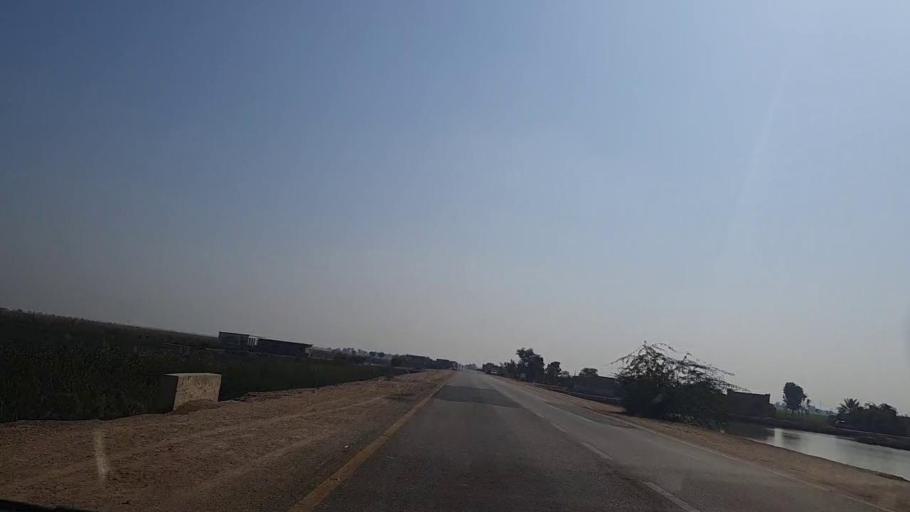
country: PK
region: Sindh
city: Sakrand
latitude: 26.0762
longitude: 68.4047
